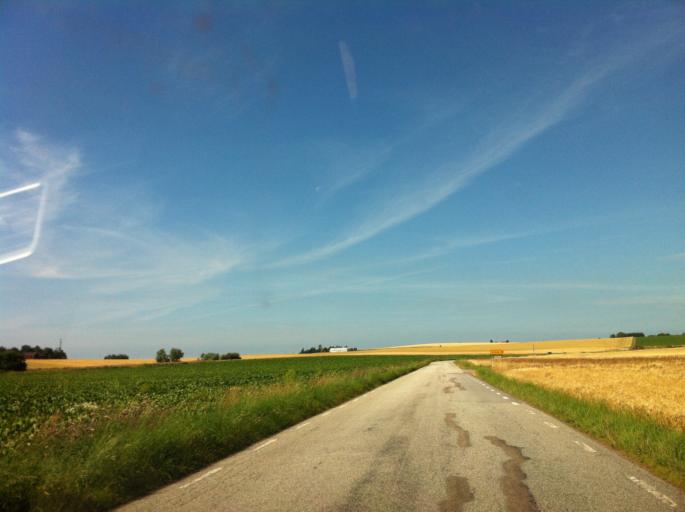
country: SE
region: Skane
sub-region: Landskrona
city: Asmundtorp
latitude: 55.9239
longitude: 12.9033
